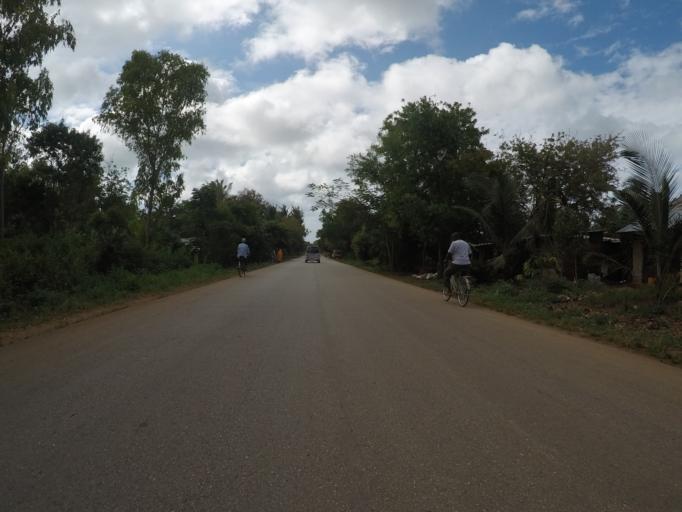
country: TZ
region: Zanzibar North
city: Nungwi
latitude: -5.7860
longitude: 39.3003
